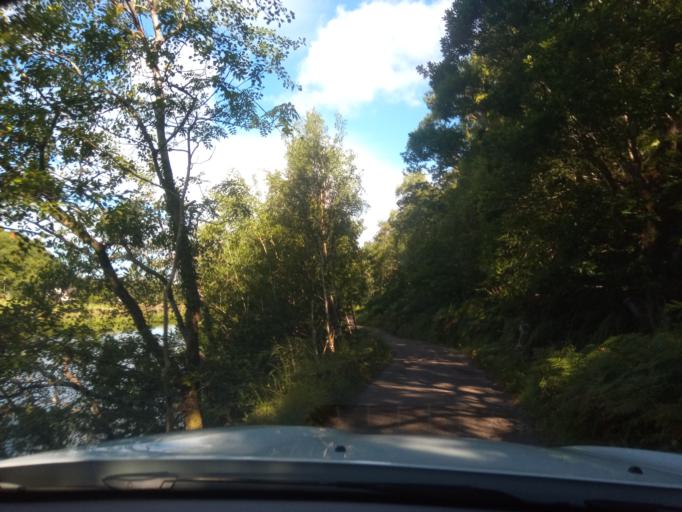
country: GB
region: Scotland
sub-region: Argyll and Bute
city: Isle Of Mull
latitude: 56.7631
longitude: -5.8194
